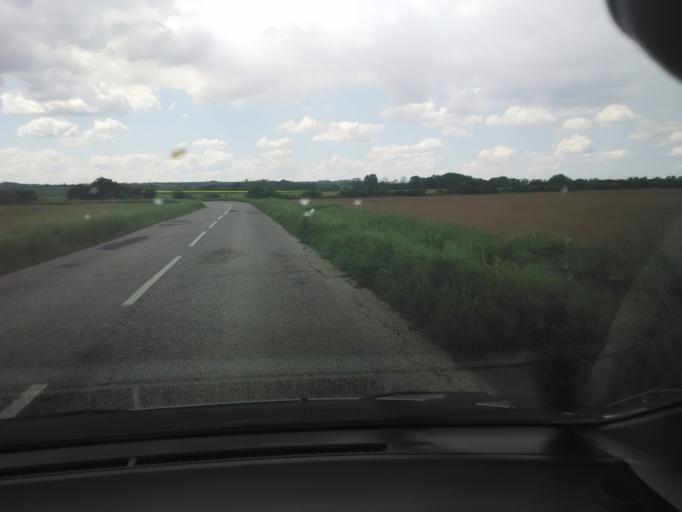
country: SK
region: Nitriansky
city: Levice
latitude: 48.1328
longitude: 18.4936
